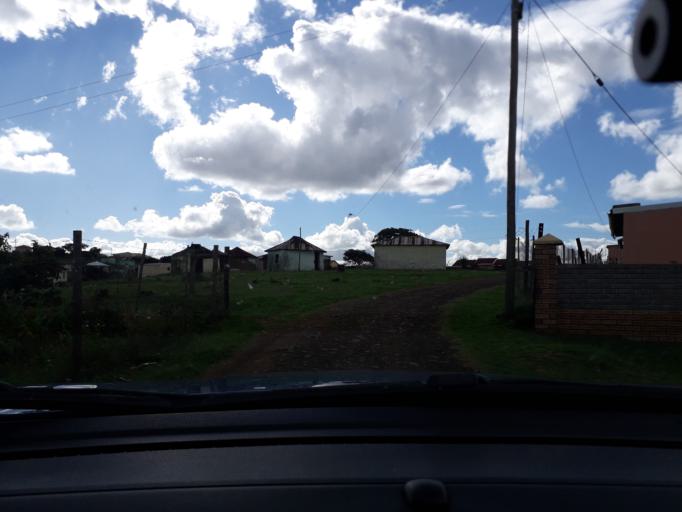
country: ZA
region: Eastern Cape
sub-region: Buffalo City Metropolitan Municipality
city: Bhisho
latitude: -33.1165
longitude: 27.4299
